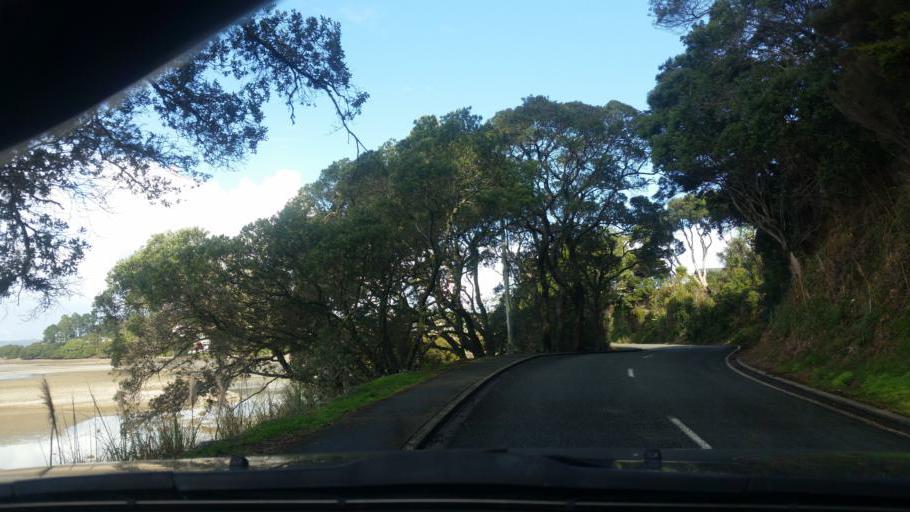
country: NZ
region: Auckland
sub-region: Auckland
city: Wellsford
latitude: -36.2515
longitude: 174.2479
